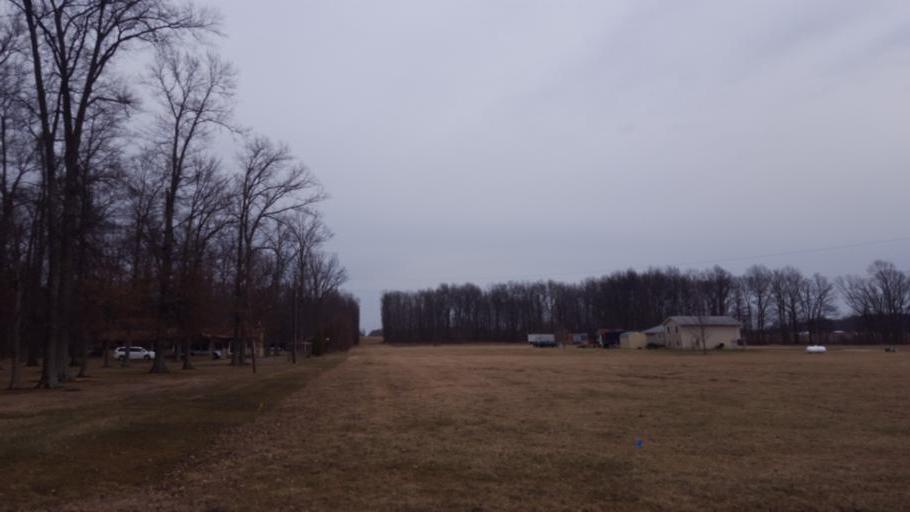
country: US
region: Ohio
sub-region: Crawford County
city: Galion
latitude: 40.6903
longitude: -82.7935
